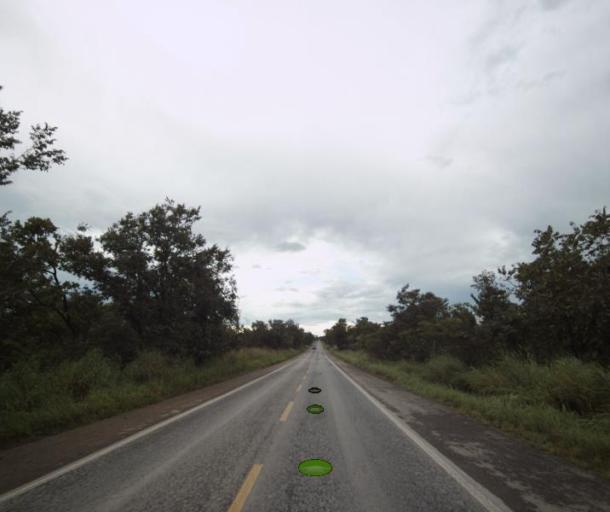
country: BR
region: Goias
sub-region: Porangatu
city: Porangatu
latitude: -13.6714
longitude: -49.0281
